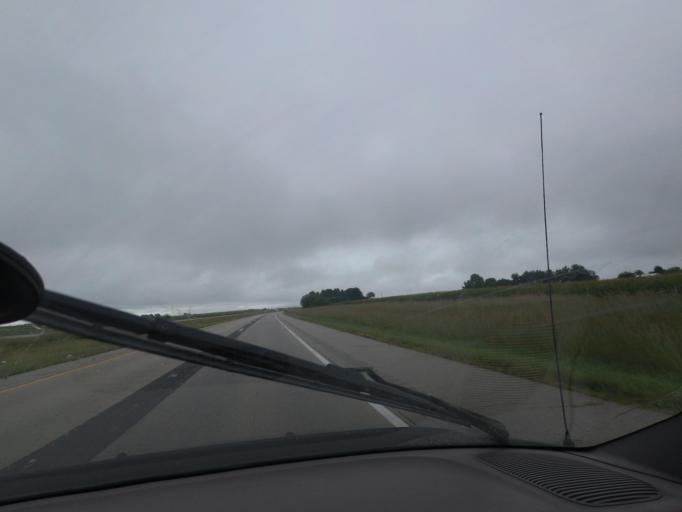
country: US
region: Illinois
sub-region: Sangamon County
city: Riverton
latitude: 39.8394
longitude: -89.3714
